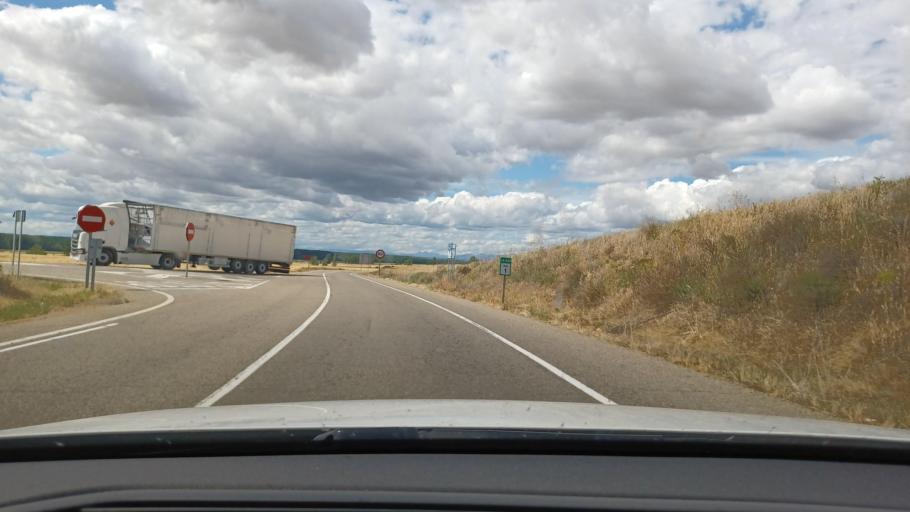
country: ES
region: Castille and Leon
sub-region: Provincia de Leon
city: Sahagun
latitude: 42.3795
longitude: -5.0269
